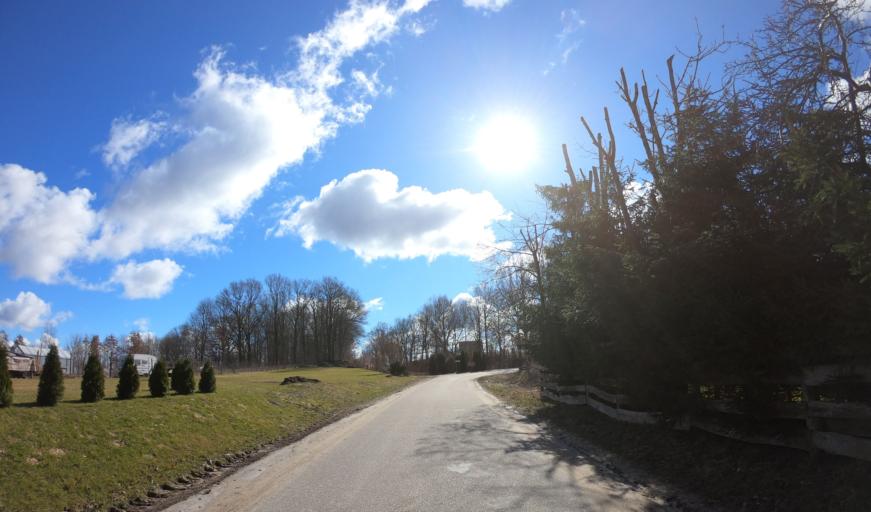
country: PL
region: West Pomeranian Voivodeship
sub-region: Powiat drawski
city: Zlocieniec
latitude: 53.4751
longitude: 15.9726
